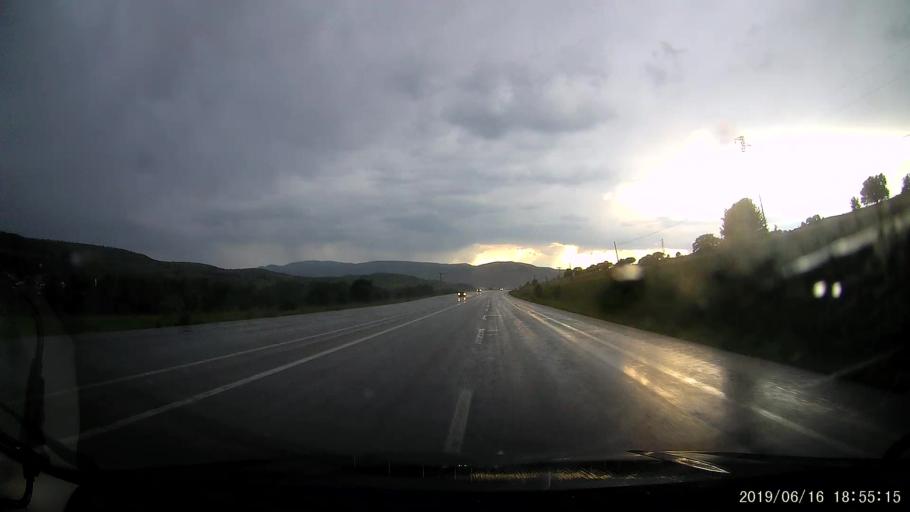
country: TR
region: Erzincan
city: Refahiye
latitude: 39.8993
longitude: 38.8328
